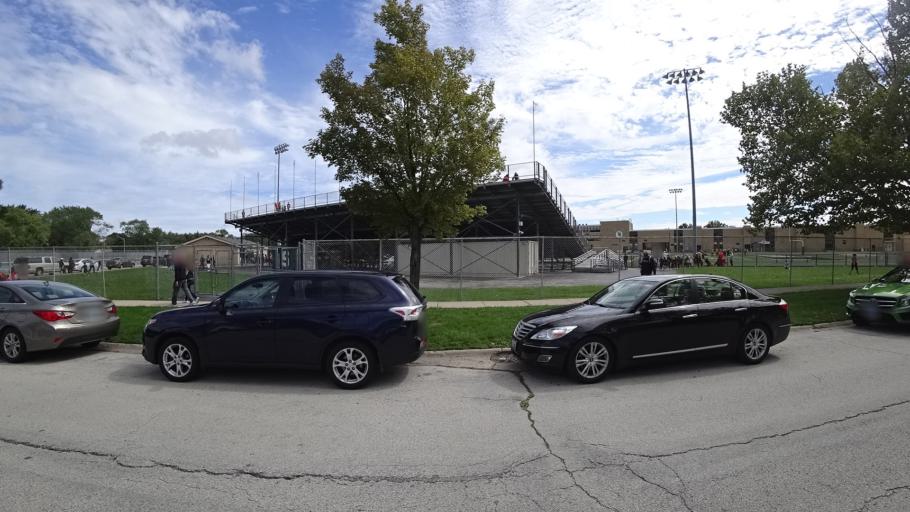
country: US
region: Illinois
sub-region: Cook County
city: Burbank
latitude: 41.7223
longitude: -87.7702
